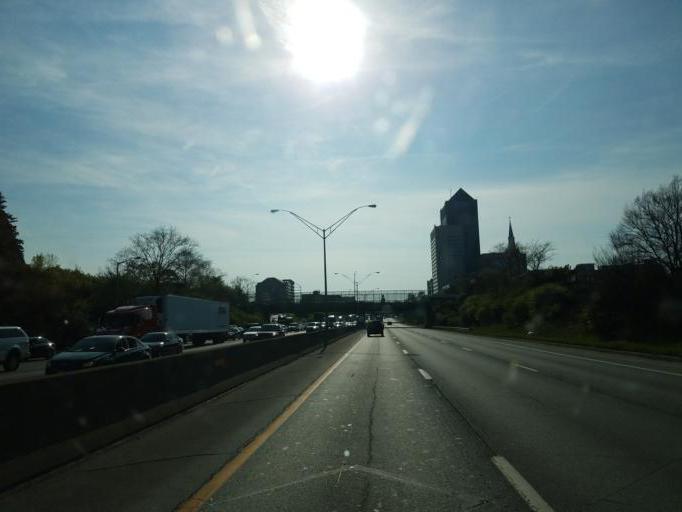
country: US
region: Ohio
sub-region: Franklin County
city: Columbus
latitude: 39.9537
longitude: -82.9926
